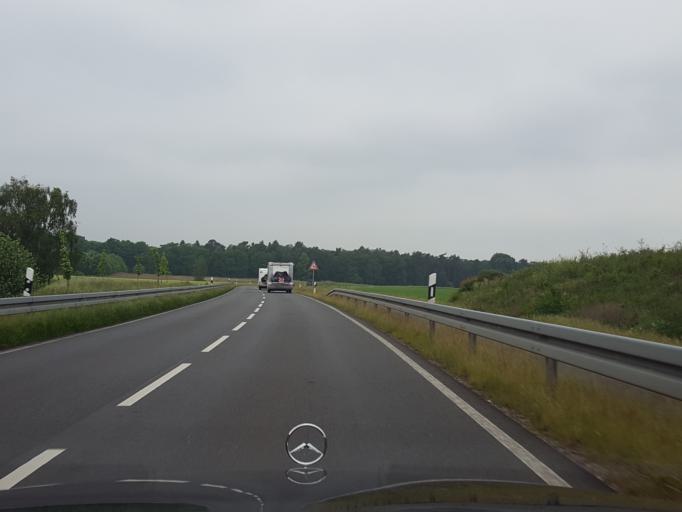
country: DE
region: North Rhine-Westphalia
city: Olfen
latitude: 51.7042
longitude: 7.3602
